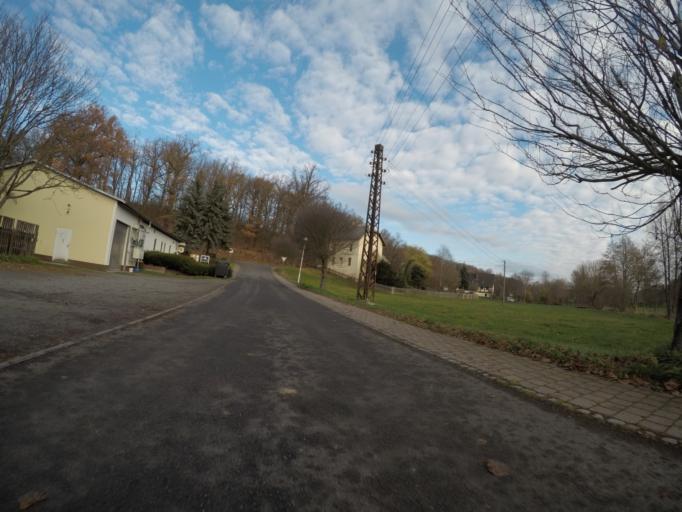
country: DE
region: Thuringia
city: Vollmershain
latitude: 50.8529
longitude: 12.2893
